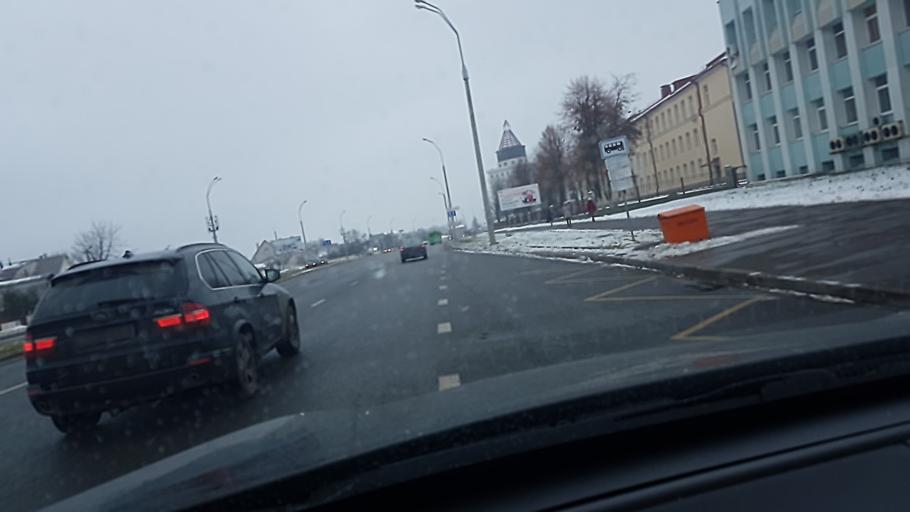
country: BY
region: Minsk
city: Bal'shavik
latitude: 53.9533
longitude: 27.5351
